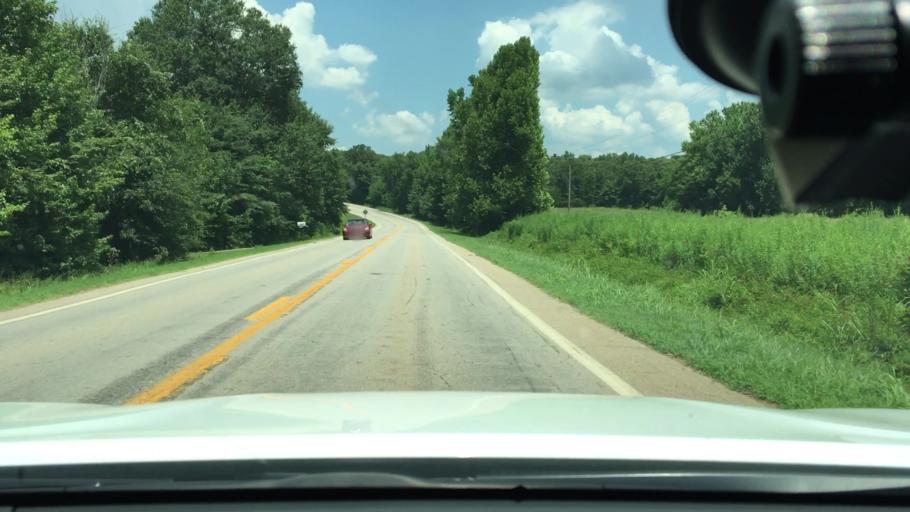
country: US
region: Arkansas
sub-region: Logan County
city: Booneville
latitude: 35.2062
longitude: -93.9244
